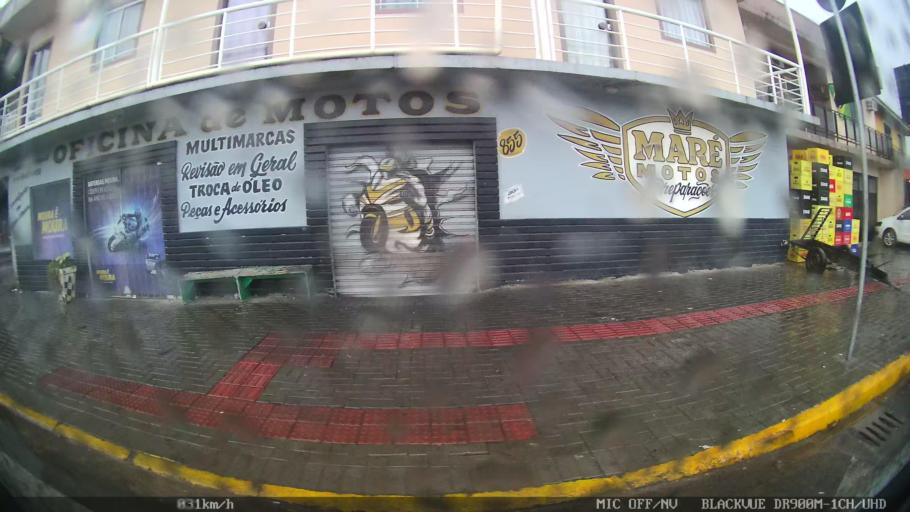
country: BR
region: Santa Catarina
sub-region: Navegantes
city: Navegantes
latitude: -26.8849
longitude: -48.6534
